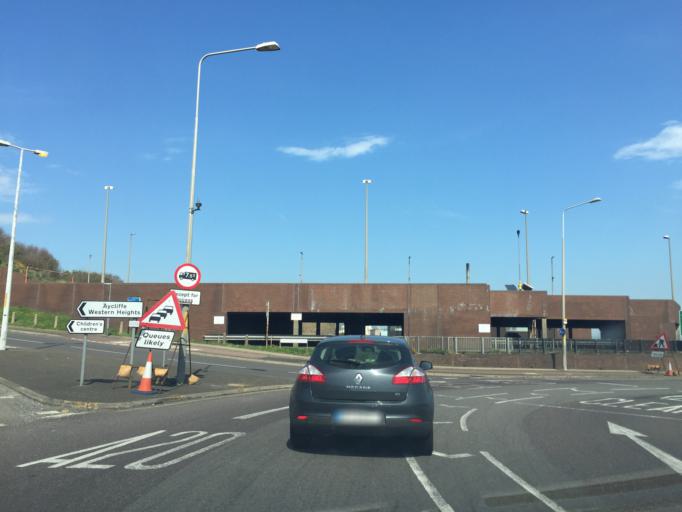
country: GB
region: England
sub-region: Kent
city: Dover
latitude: 51.1146
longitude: 1.3030
